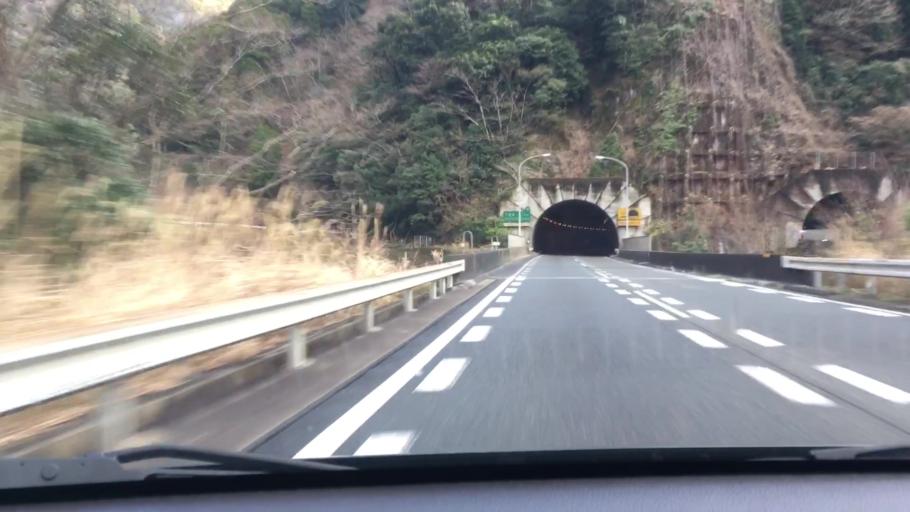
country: JP
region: Kumamoto
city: Hitoyoshi
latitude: 32.3320
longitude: 130.7425
